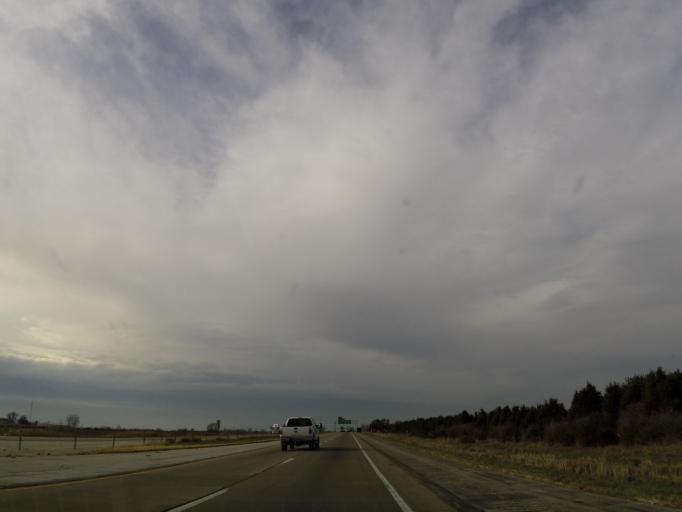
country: US
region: Iowa
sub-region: Scott County
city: Eldridge
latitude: 41.6030
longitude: -90.6583
